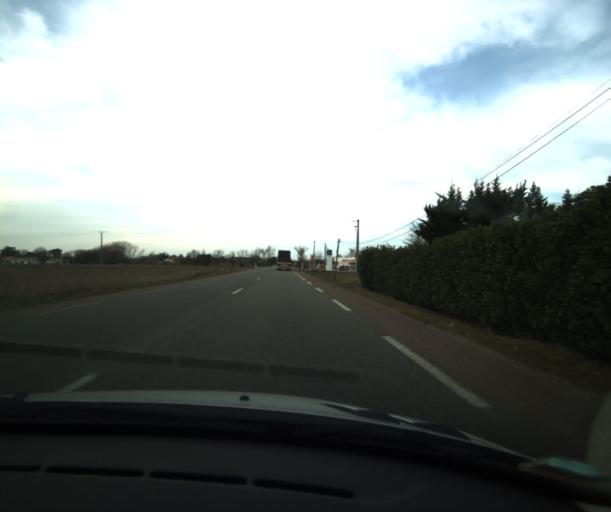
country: FR
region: Midi-Pyrenees
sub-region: Departement du Tarn-et-Garonne
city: Saint-Porquier
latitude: 43.9956
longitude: 1.1876
